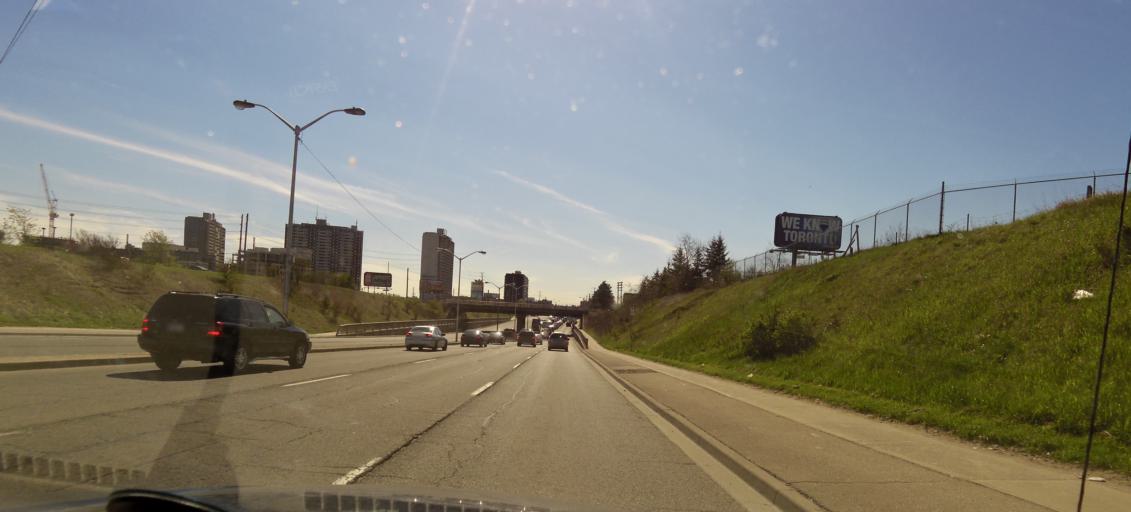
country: CA
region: Ontario
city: Concord
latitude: 43.7530
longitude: -79.5382
